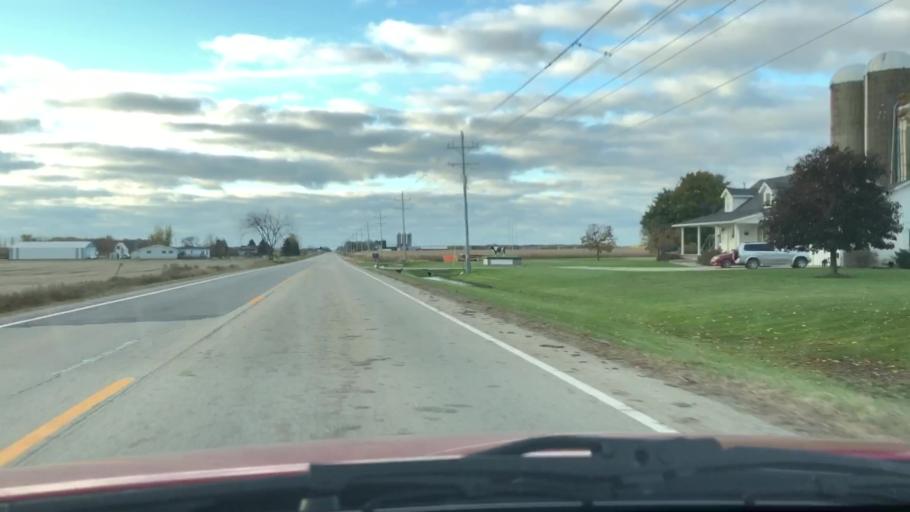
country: US
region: Wisconsin
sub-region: Outagamie County
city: Seymour
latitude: 44.4513
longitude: -88.2913
